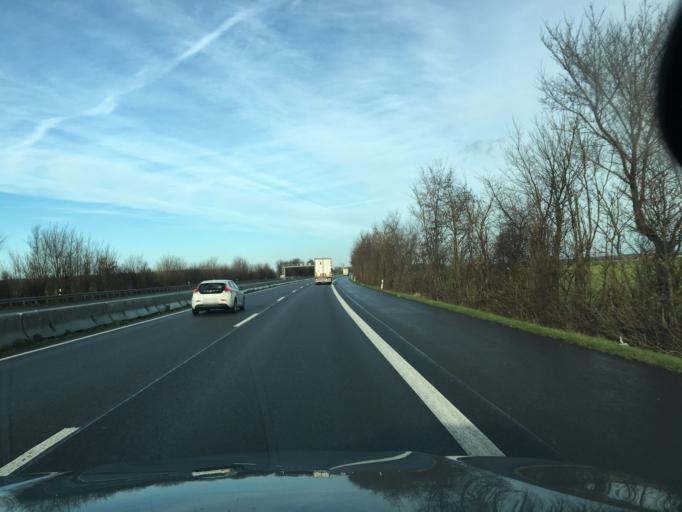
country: DE
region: North Rhine-Westphalia
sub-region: Regierungsbezirk Koln
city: Rheinbach
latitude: 50.6548
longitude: 6.9273
